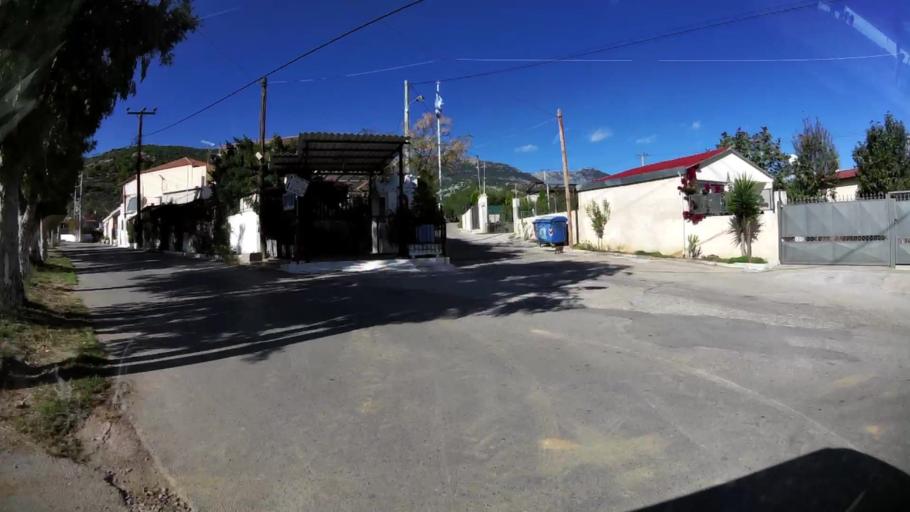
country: GR
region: Attica
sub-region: Nomarchia Anatolikis Attikis
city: Acharnes
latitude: 38.1078
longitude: 23.7224
